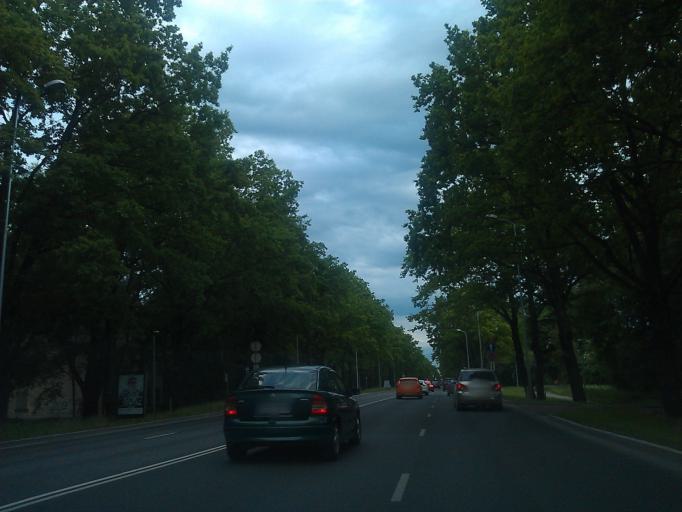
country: LV
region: Marupe
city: Marupe
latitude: 56.9039
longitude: 24.0816
